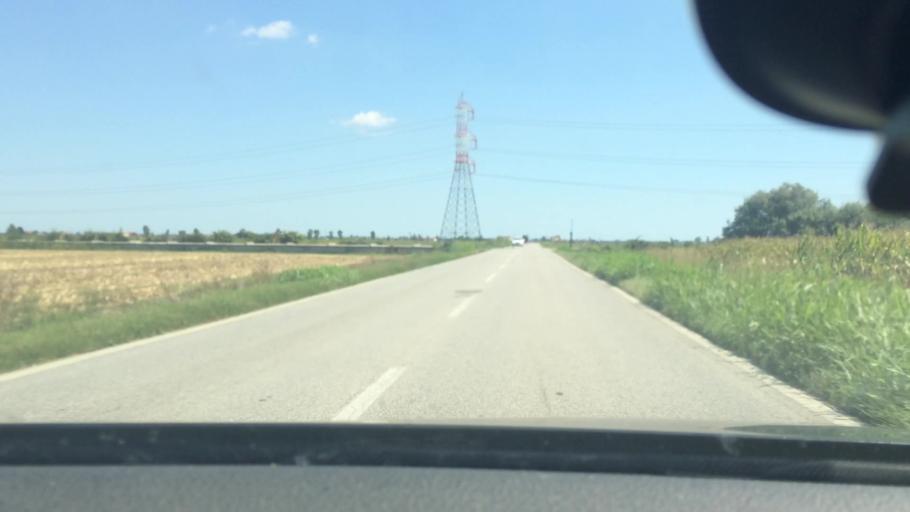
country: IT
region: Emilia-Romagna
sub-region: Provincia di Ferrara
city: Lagosanto
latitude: 44.7600
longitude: 12.0787
